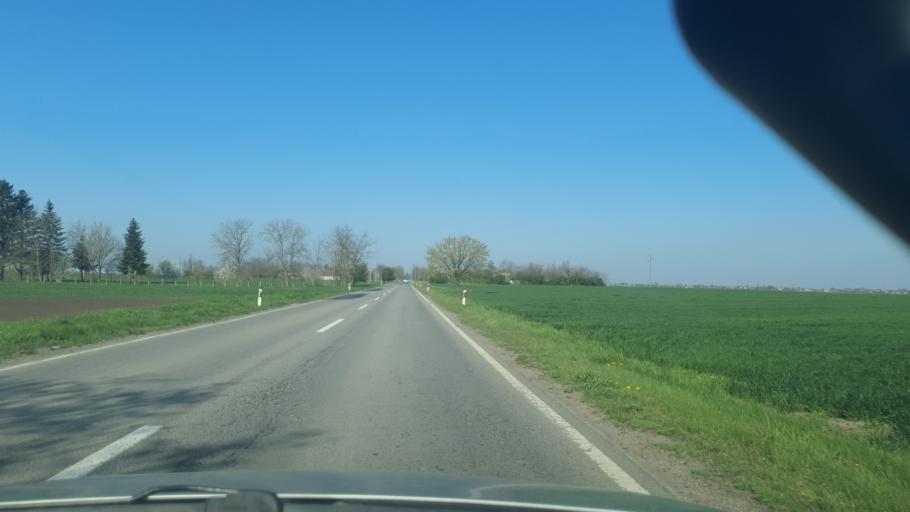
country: RS
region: Autonomna Pokrajina Vojvodina
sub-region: Zapadnobacki Okrug
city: Sombor
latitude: 45.7680
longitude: 19.2172
